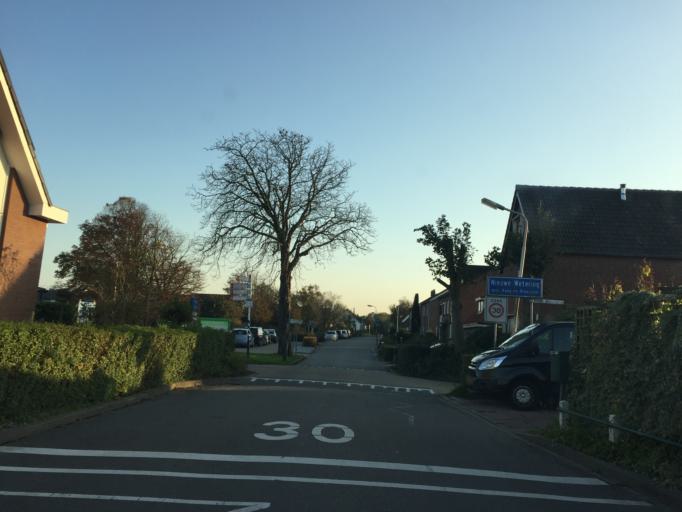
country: NL
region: South Holland
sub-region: Gemeente Kaag en Braassem
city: Oude Wetering
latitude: 52.2146
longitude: 4.6205
